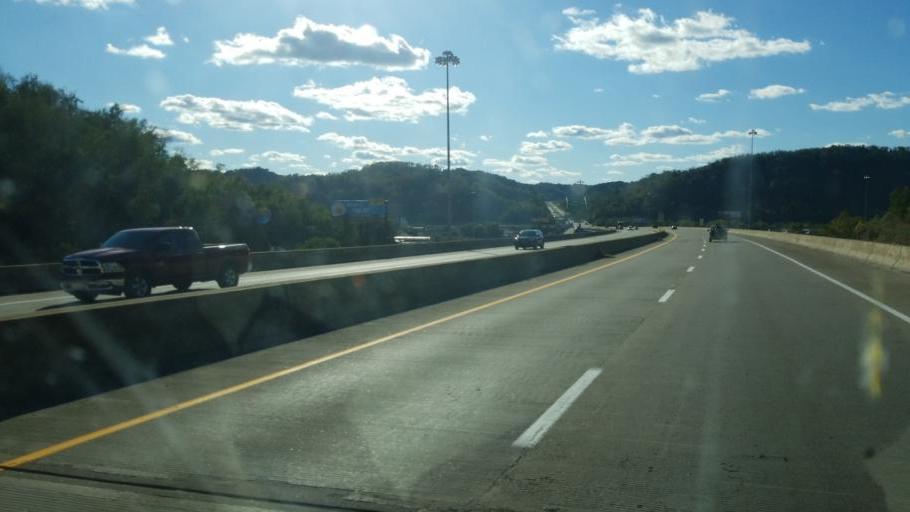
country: US
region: West Virginia
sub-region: Ohio County
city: Wheeling
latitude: 40.0516
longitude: -80.7169
